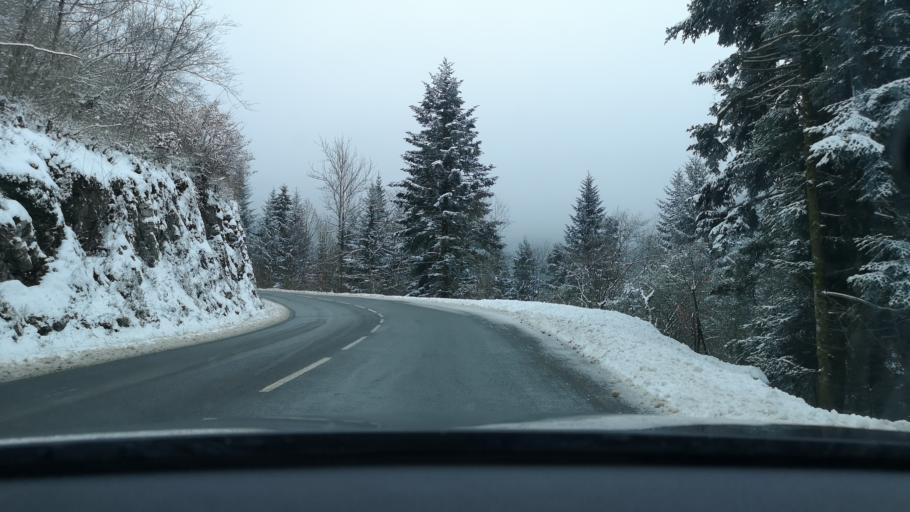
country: FR
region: Rhone-Alpes
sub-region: Departement de l'Ain
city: Oyonnax
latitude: 46.2542
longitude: 5.6955
